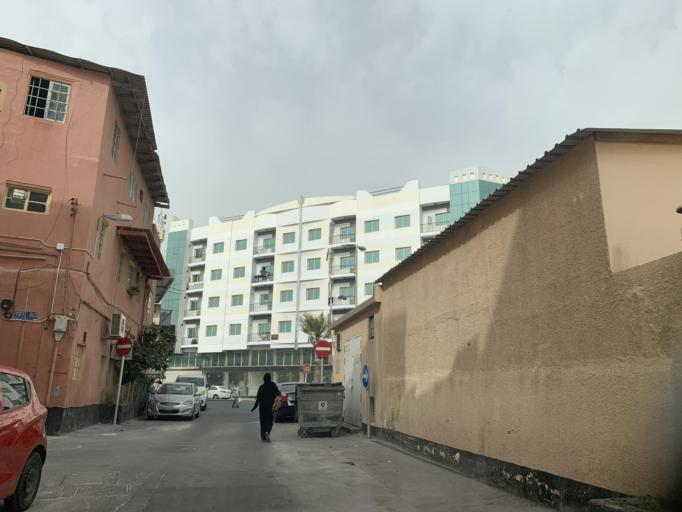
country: BH
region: Manama
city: Manama
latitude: 26.2307
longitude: 50.5821
